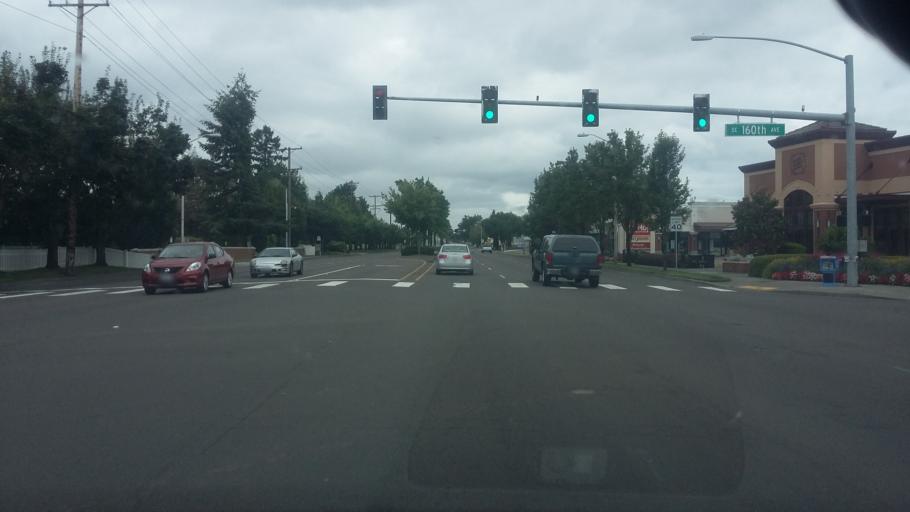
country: US
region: Washington
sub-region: Clark County
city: Mill Plain
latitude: 45.6159
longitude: -122.5074
